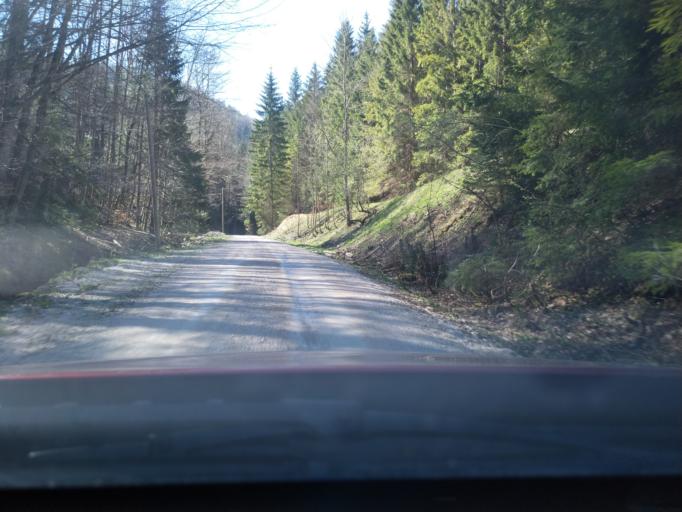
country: AT
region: Lower Austria
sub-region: Politischer Bezirk Wiener Neustadt
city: Gutenstein
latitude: 47.8166
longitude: 15.8463
